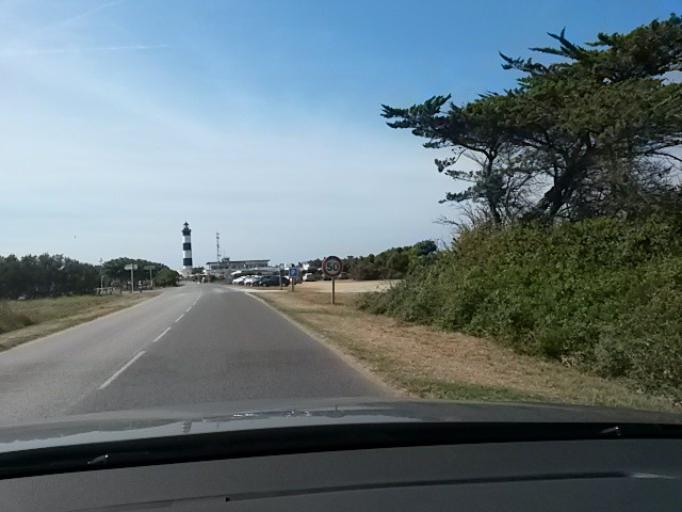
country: FR
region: Poitou-Charentes
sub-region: Departement de la Charente-Maritime
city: Saint-Denis-d'Oleron
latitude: 46.0457
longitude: -1.4043
